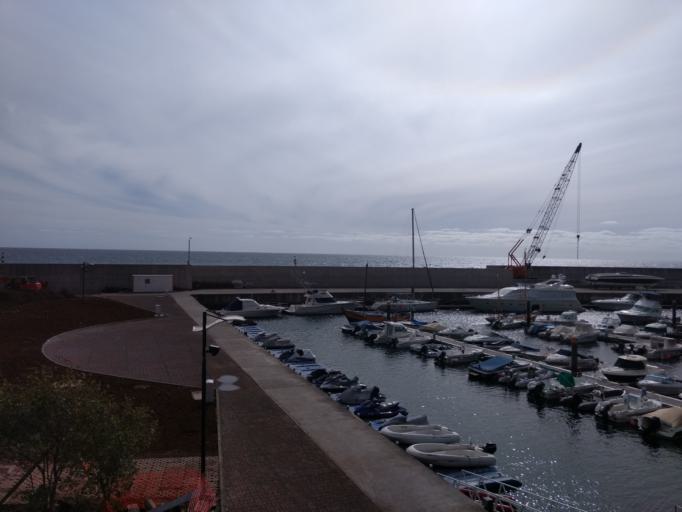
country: PT
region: Madeira
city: Calheta
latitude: 32.7177
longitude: -17.1705
